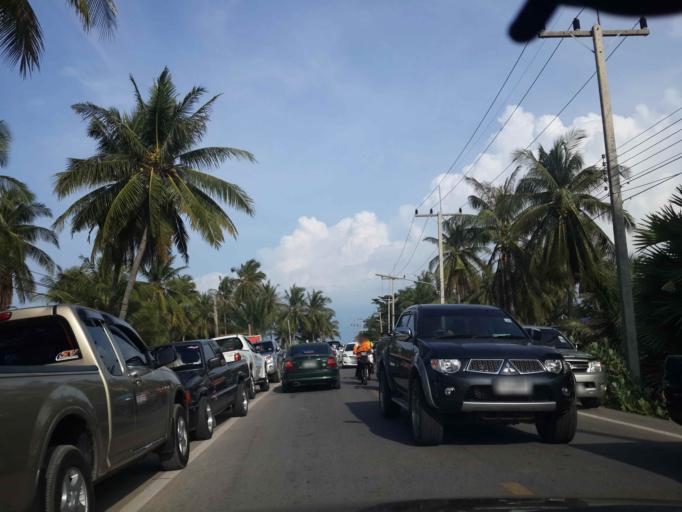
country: TH
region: Pattani
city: Yaring
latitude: 6.9291
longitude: 101.3222
